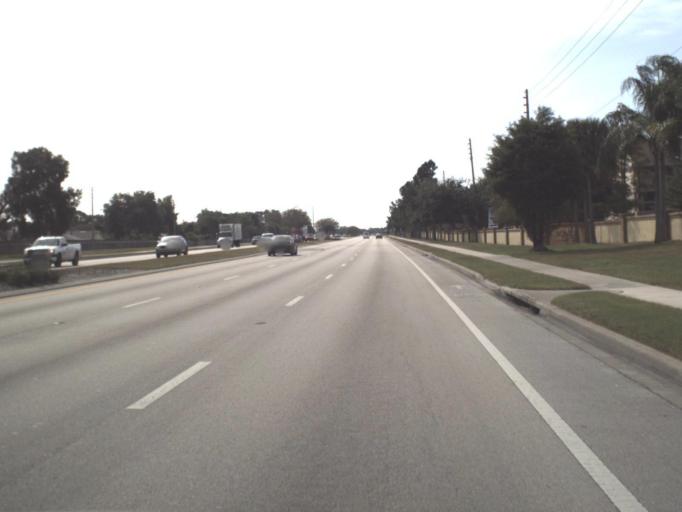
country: US
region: Florida
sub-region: Orange County
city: Oak Ridge
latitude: 28.4800
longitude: -81.4177
